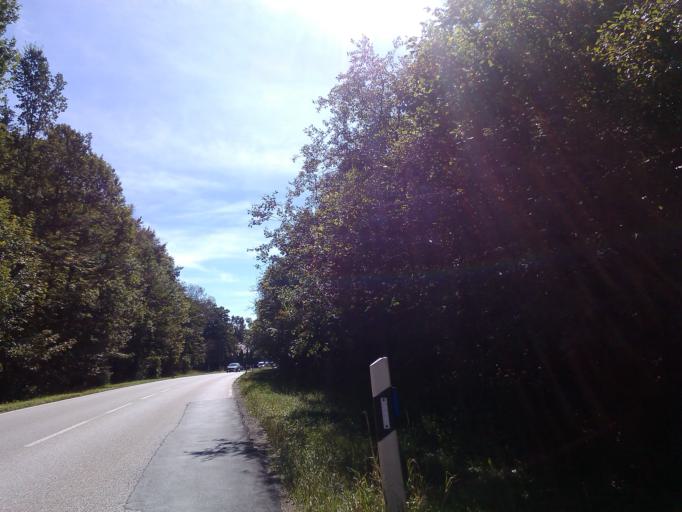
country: DE
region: Bavaria
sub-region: Upper Bavaria
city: Starnberg
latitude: 48.0166
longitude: 11.3286
